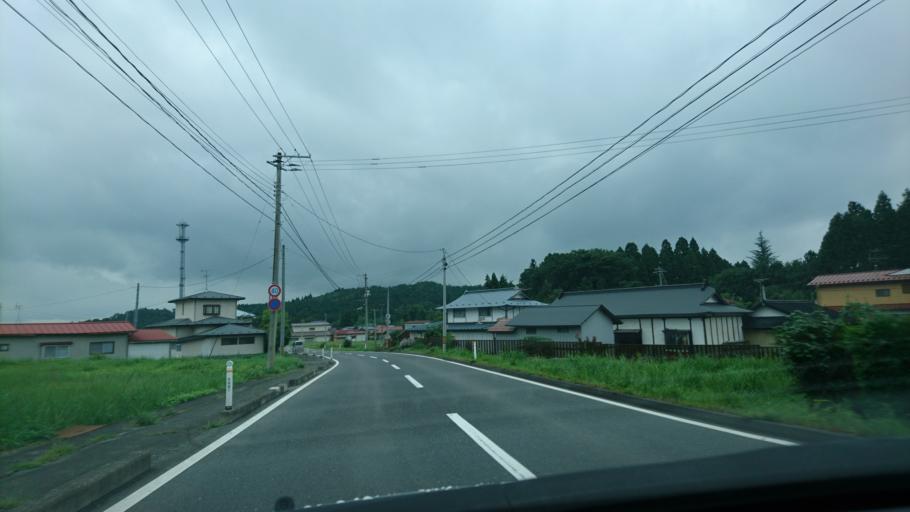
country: JP
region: Iwate
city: Ichinoseki
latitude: 38.8053
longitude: 140.9344
